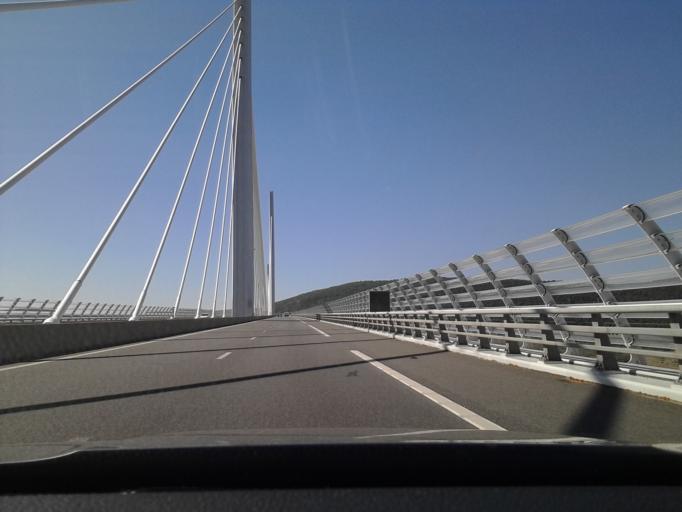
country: FR
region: Midi-Pyrenees
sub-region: Departement de l'Aveyron
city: Creissels
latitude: 44.0904
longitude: 3.0211
